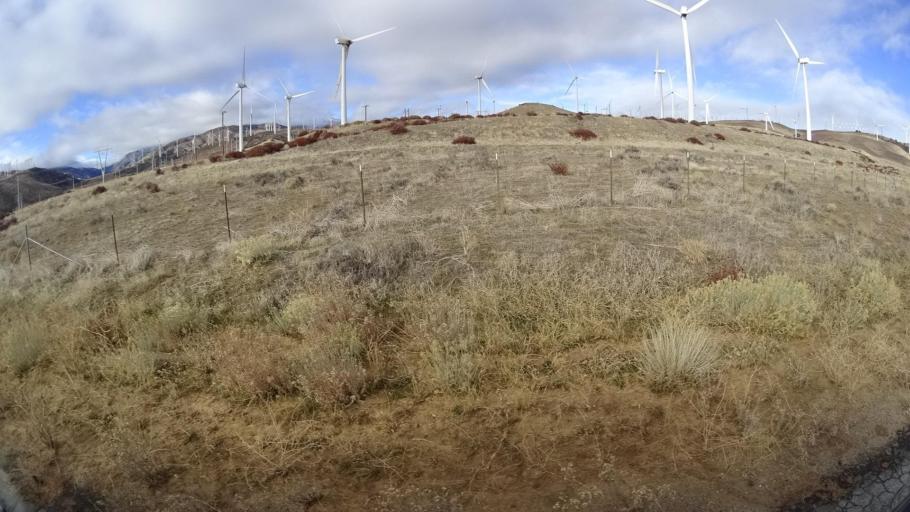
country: US
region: California
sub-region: Kern County
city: Tehachapi
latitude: 35.0550
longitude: -118.3543
